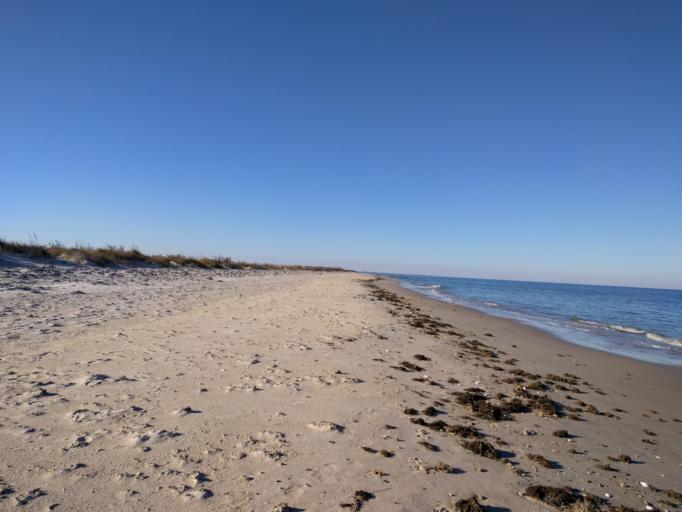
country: US
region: Virginia
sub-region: City of Poquoson
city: Poquoson
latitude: 37.0976
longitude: -76.2770
